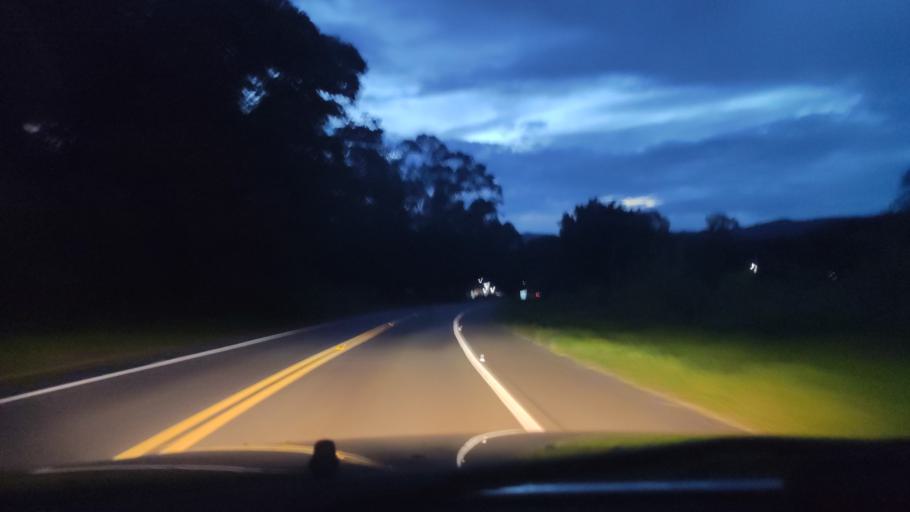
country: BR
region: Sao Paulo
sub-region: Socorro
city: Socorro
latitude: -22.5600
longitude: -46.5893
